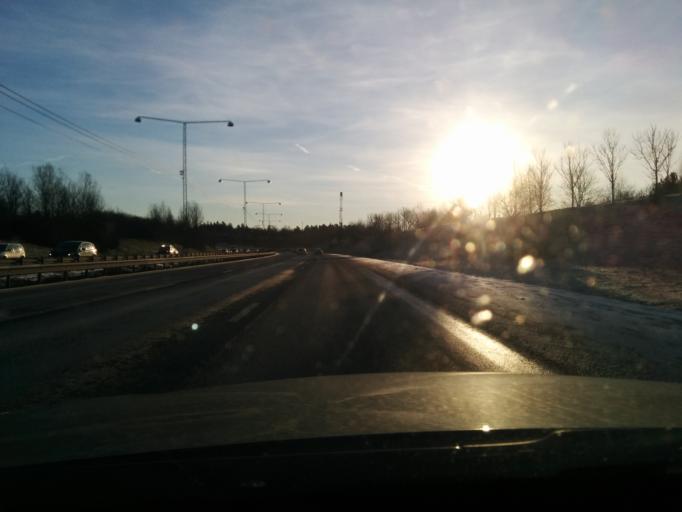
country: SE
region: Stockholm
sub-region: Sollentuna Kommun
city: Sollentuna
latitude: 59.4621
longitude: 17.9107
